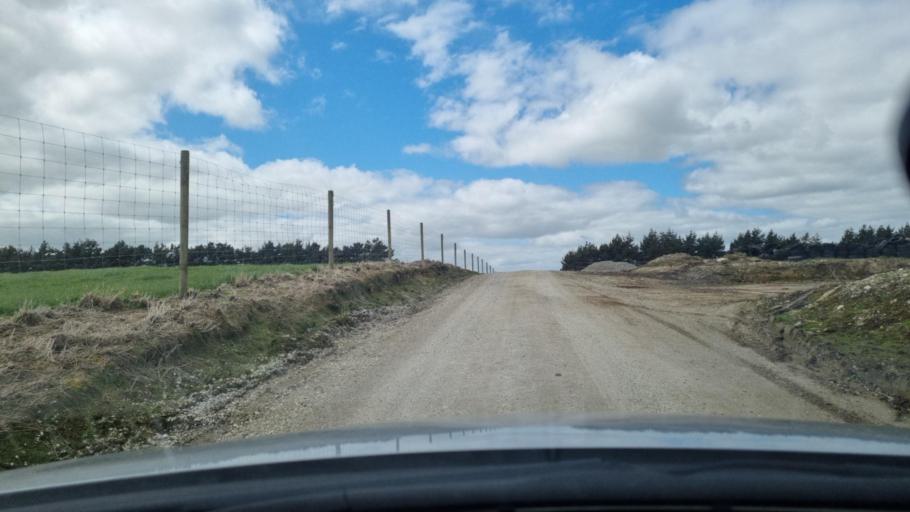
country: NZ
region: Southland
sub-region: Invercargill City
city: Invercargill
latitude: -46.4557
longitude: 168.4233
